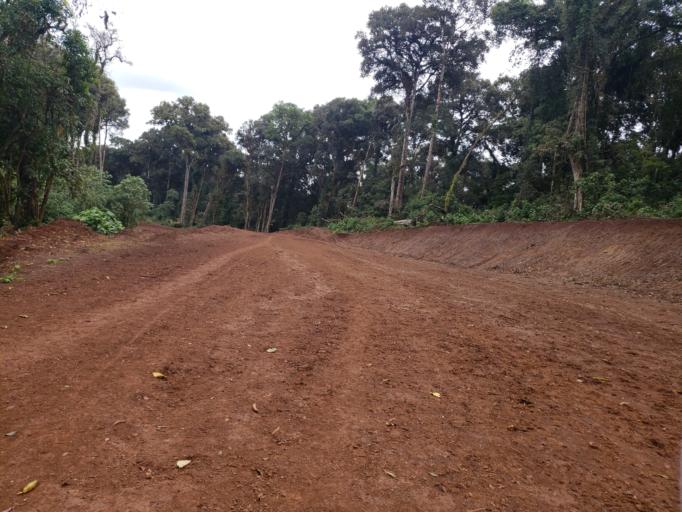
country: ET
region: Oromiya
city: Dodola
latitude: 6.5886
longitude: 39.4121
